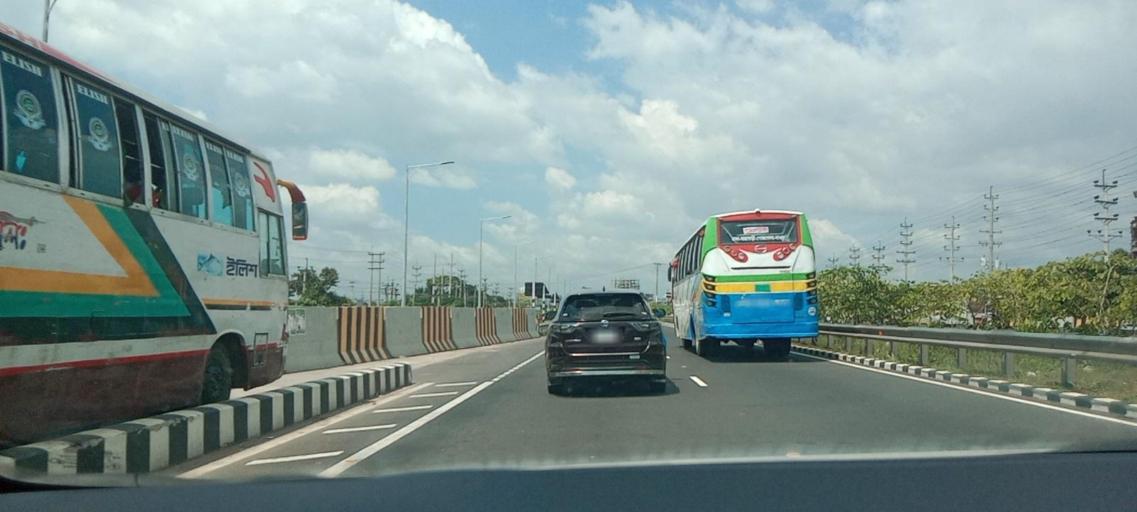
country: BD
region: Dhaka
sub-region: Dhaka
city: Dhaka
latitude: 23.6787
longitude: 90.4098
